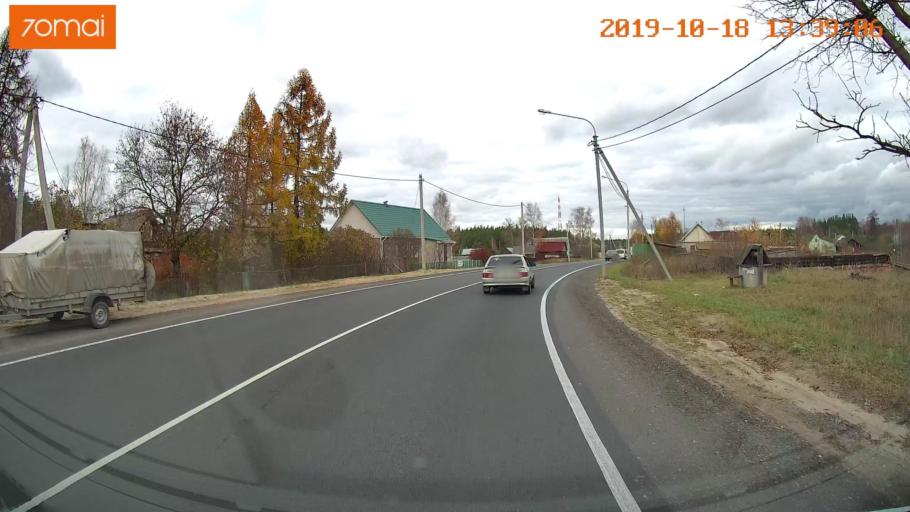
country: RU
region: Rjazan
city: Solotcha
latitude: 54.8956
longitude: 40.0002
